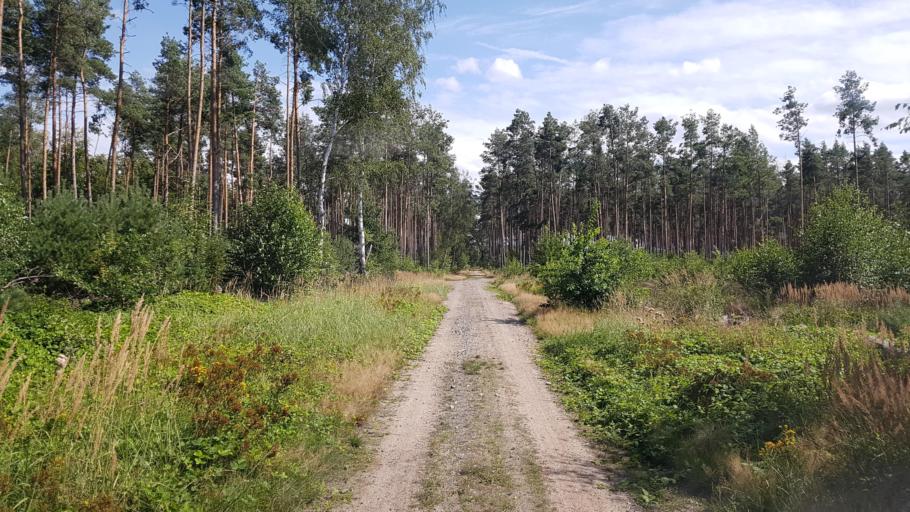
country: DE
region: Brandenburg
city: Bad Liebenwerda
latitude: 51.4939
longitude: 13.3109
